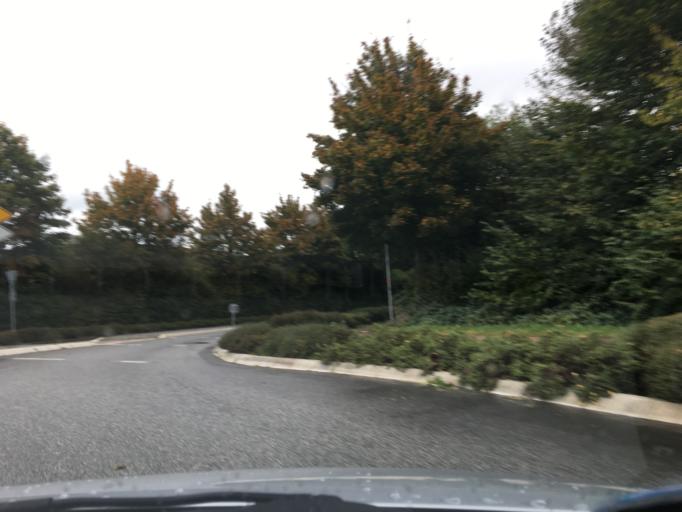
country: DE
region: Schleswig-Holstein
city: Gettorf
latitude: 54.4145
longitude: 9.9766
